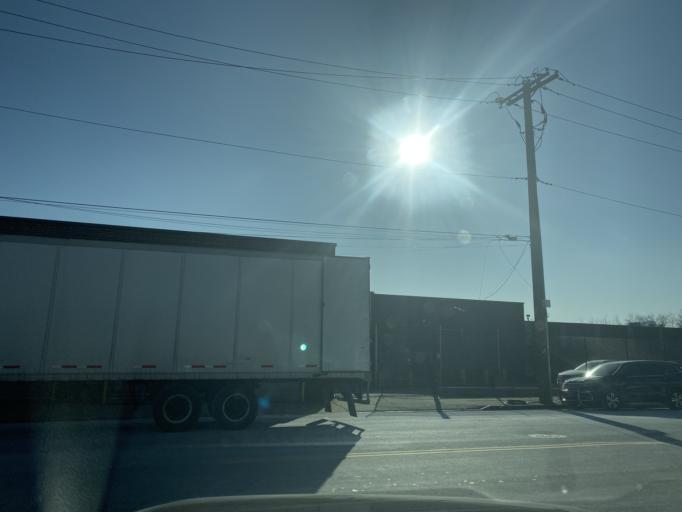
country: US
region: New York
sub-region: Bronx
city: The Bronx
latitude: 40.8330
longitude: -73.8423
